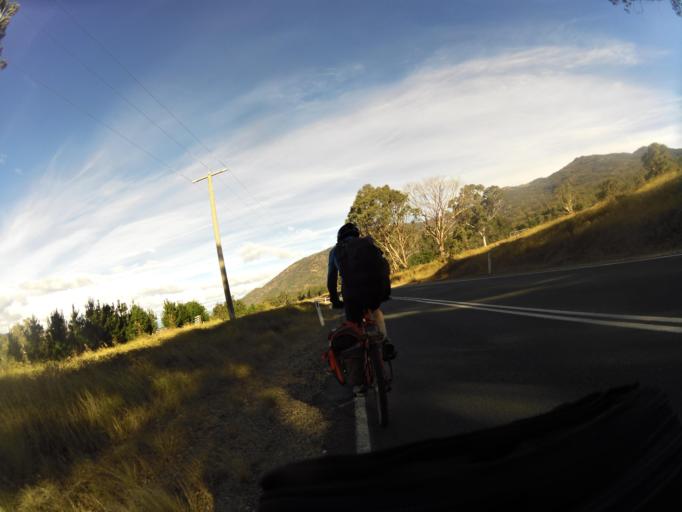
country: AU
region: New South Wales
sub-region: Greater Hume Shire
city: Holbrook
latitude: -35.9808
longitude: 147.8175
